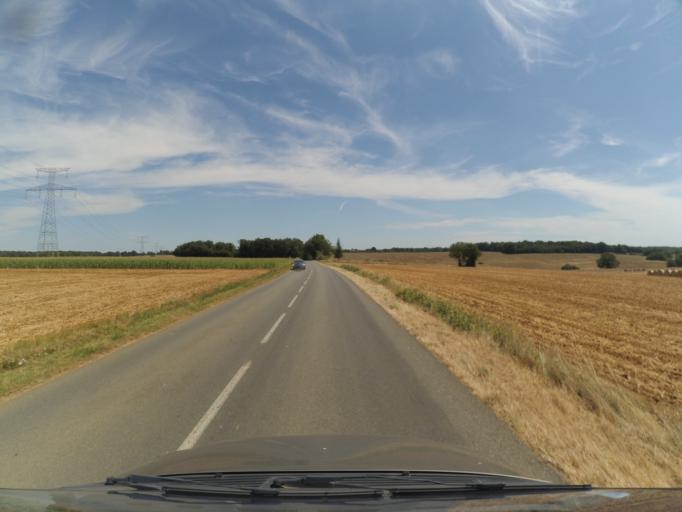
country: FR
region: Poitou-Charentes
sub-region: Departement de la Vienne
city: Saint-Maurice-la-Clouere
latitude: 46.3955
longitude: 0.3765
